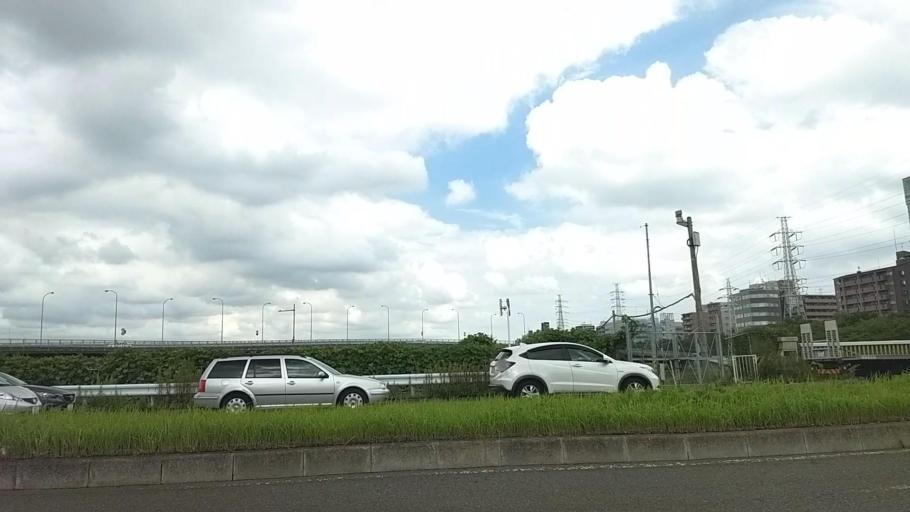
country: JP
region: Kanagawa
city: Yokohama
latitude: 35.5118
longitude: 139.6140
